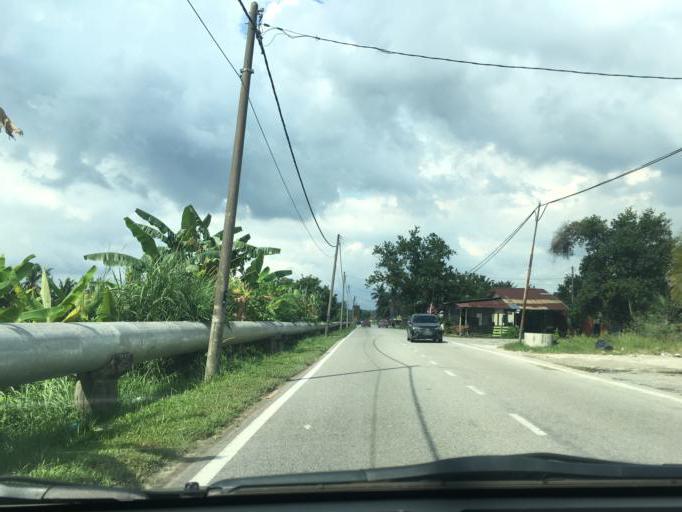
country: MY
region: Selangor
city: Kampung Baru Subang
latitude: 3.1421
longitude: 101.4473
